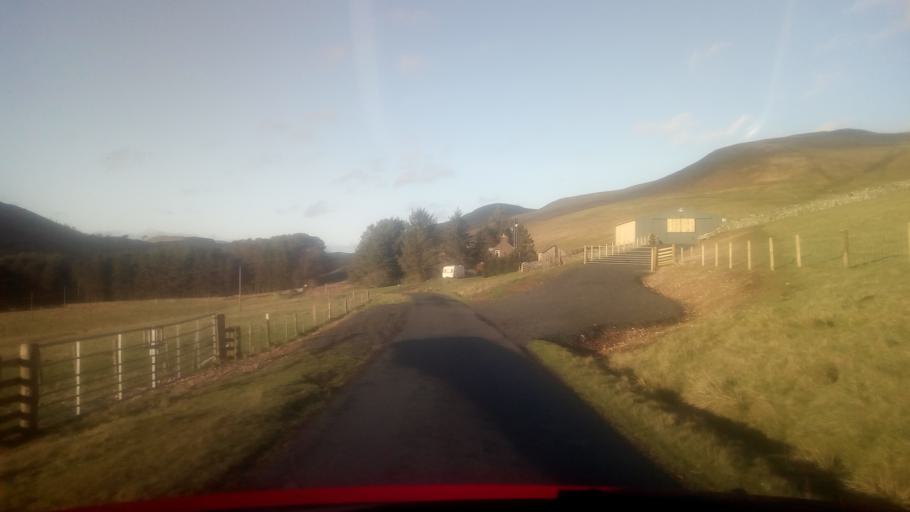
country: GB
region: Scotland
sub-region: The Scottish Borders
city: Kelso
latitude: 55.4362
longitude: -2.3636
